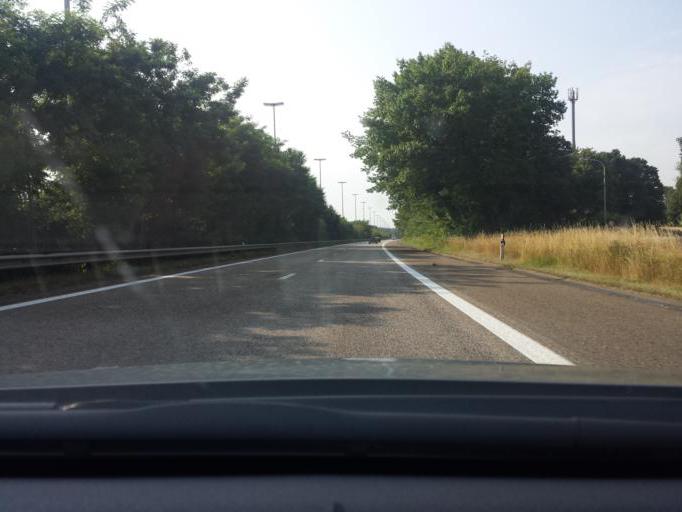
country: BE
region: Flanders
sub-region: Provincie Limburg
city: Hoeselt
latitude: 50.8633
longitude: 5.4963
